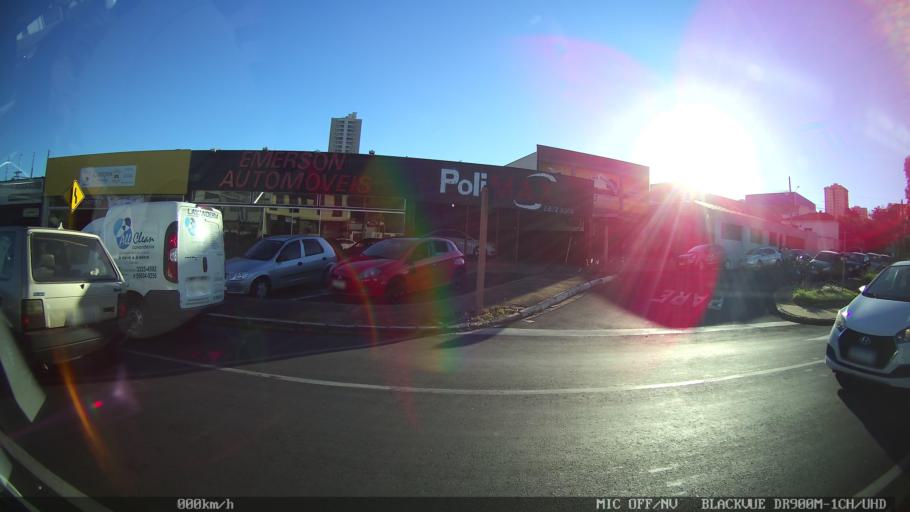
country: BR
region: Sao Paulo
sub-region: Araraquara
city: Araraquara
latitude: -21.8011
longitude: -48.1732
